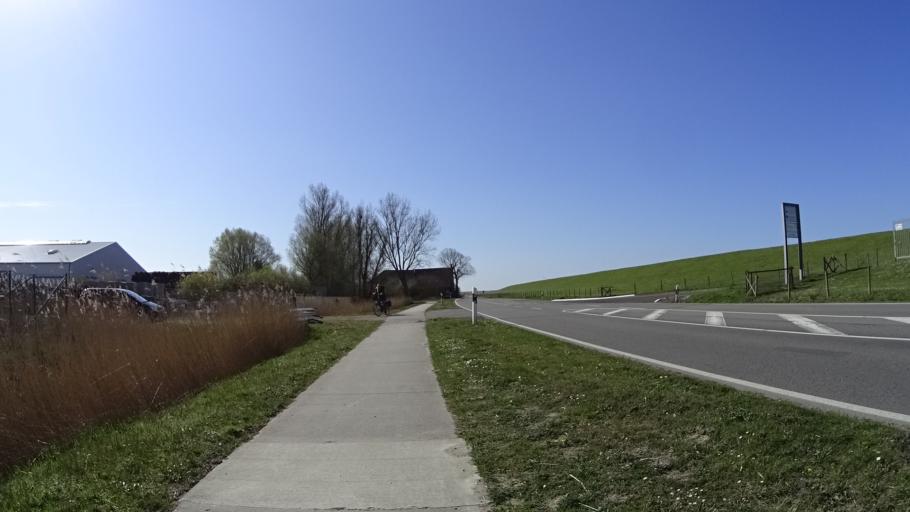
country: DE
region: Lower Saxony
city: Jemgum
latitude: 53.2644
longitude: 7.4074
